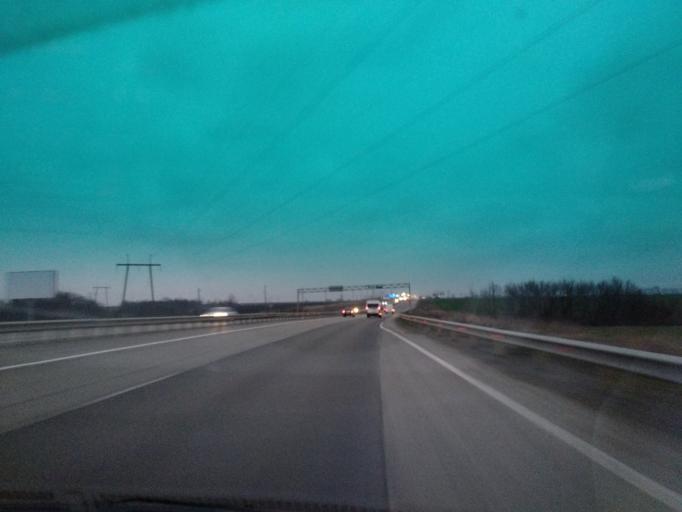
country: RU
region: Adygeya
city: Adygeysk
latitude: 44.8657
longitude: 39.1910
